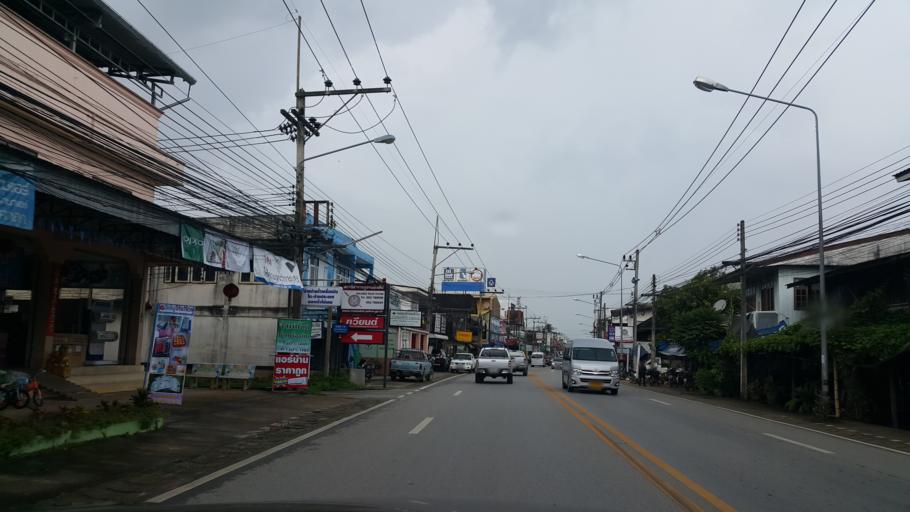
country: TH
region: Lampang
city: Wang Nuea
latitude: 19.2024
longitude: 99.5170
